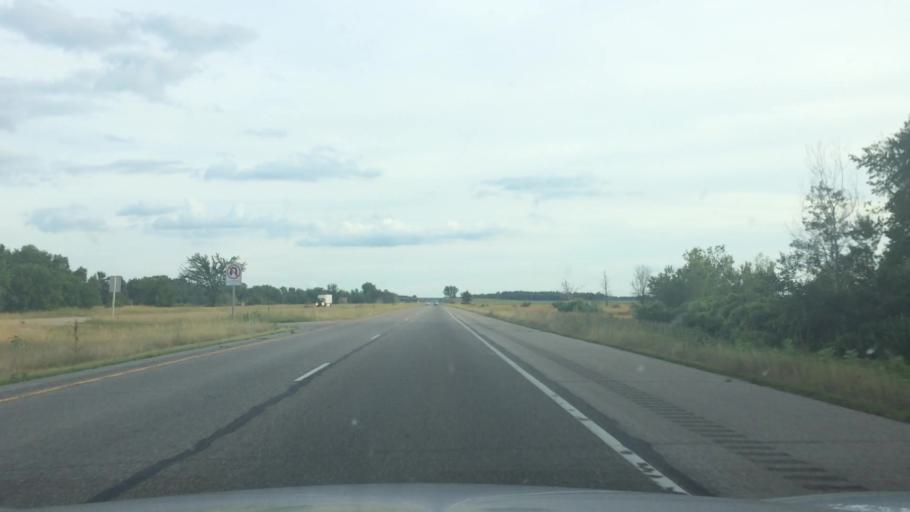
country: US
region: Wisconsin
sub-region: Waushara County
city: Wautoma
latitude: 44.1661
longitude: -89.5327
